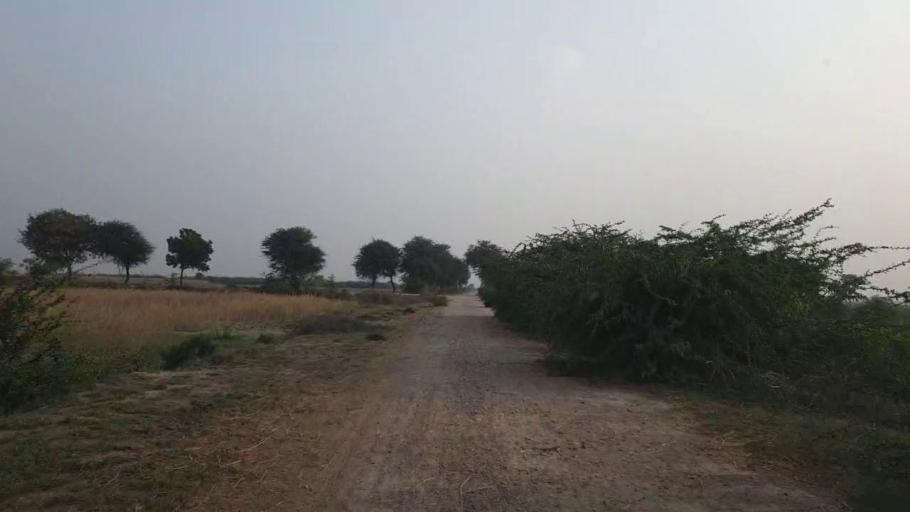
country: PK
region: Sindh
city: Mirpur Batoro
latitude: 24.6525
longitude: 68.3726
